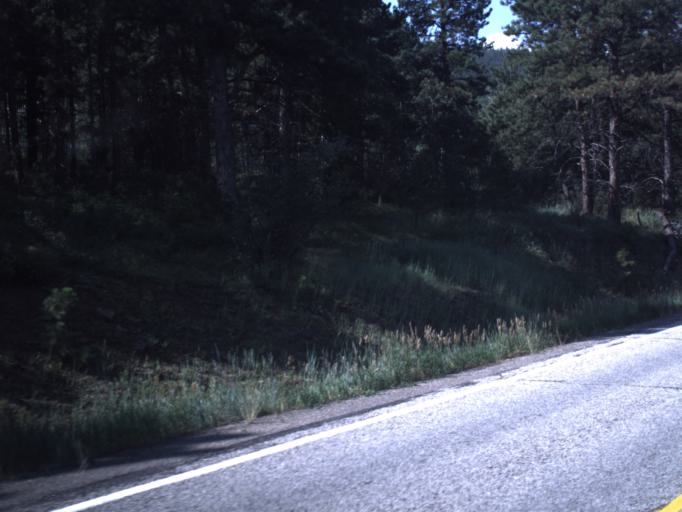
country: US
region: Utah
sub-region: Daggett County
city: Manila
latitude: 40.8632
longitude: -109.5252
